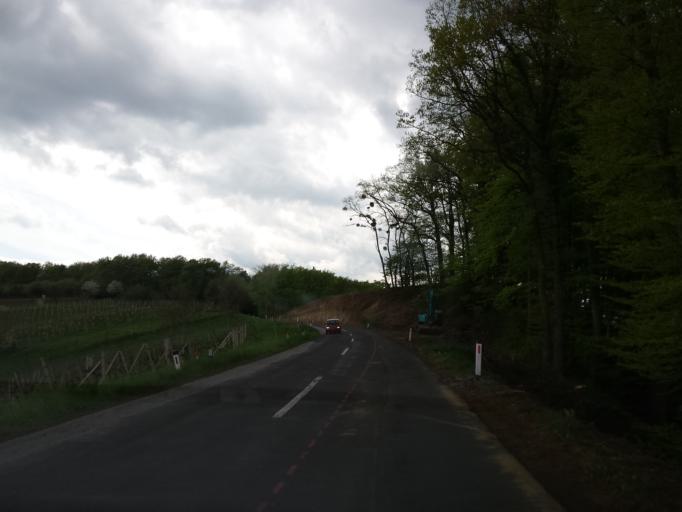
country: AT
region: Styria
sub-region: Politischer Bezirk Hartberg-Fuerstenfeld
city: UEbersbach
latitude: 47.0108
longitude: 16.0357
